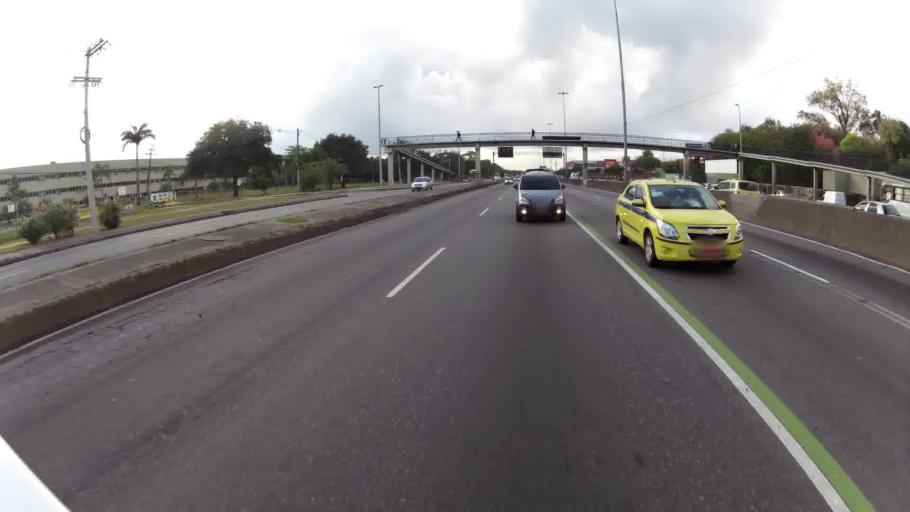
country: BR
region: Rio de Janeiro
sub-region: Duque De Caxias
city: Duque de Caxias
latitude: -22.8330
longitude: -43.2652
